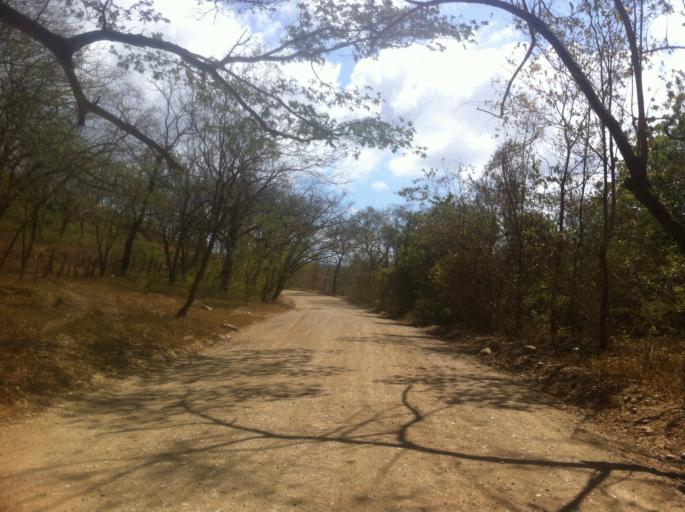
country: NI
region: Rivas
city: Tola
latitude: 11.4101
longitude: -86.0083
